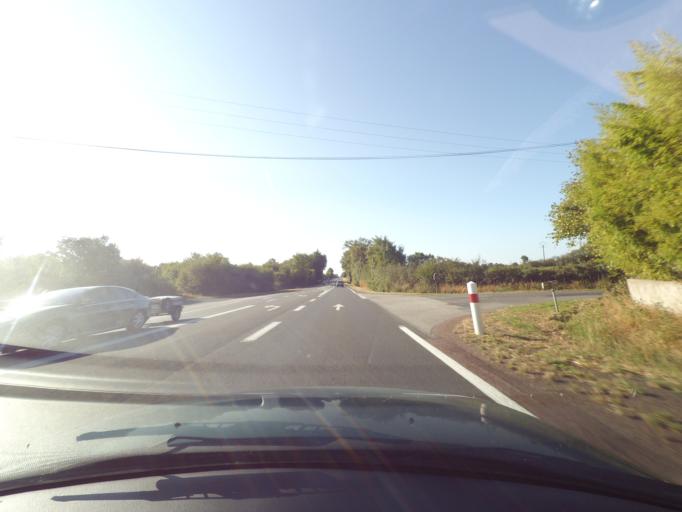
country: FR
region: Poitou-Charentes
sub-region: Departement des Deux-Sevres
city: Viennay
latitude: 46.6850
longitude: -0.2679
